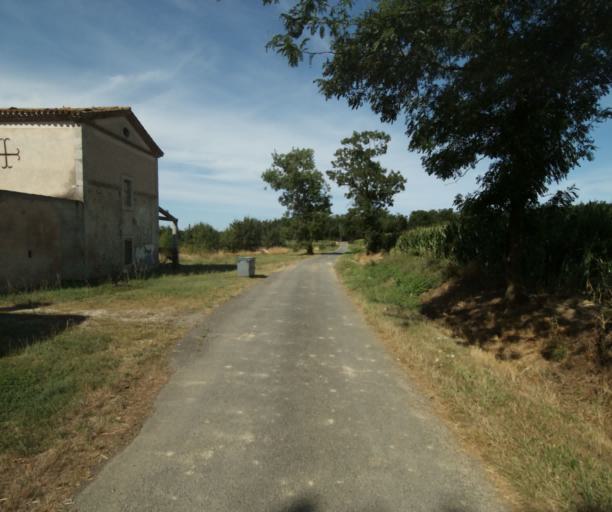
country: FR
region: Midi-Pyrenees
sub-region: Departement du Tarn
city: Soual
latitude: 43.5136
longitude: 2.0872
